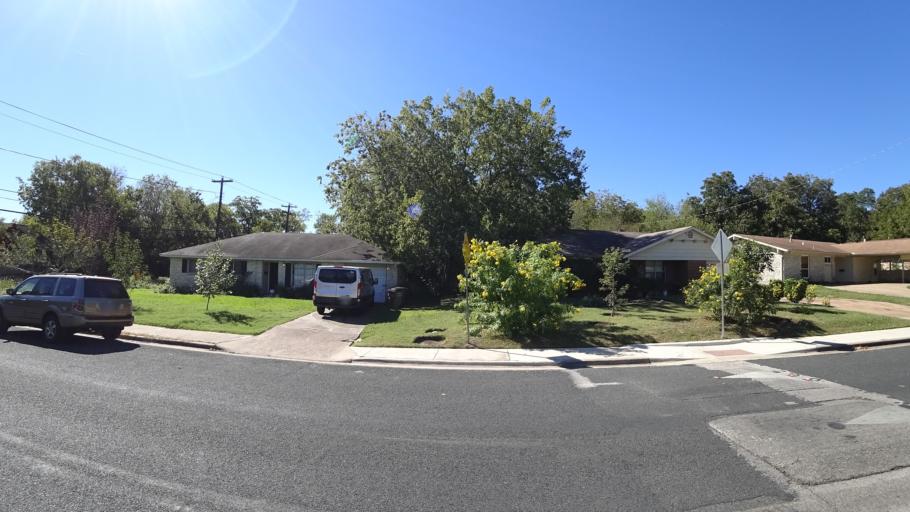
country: US
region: Texas
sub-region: Travis County
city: Austin
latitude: 30.3078
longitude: -97.6880
